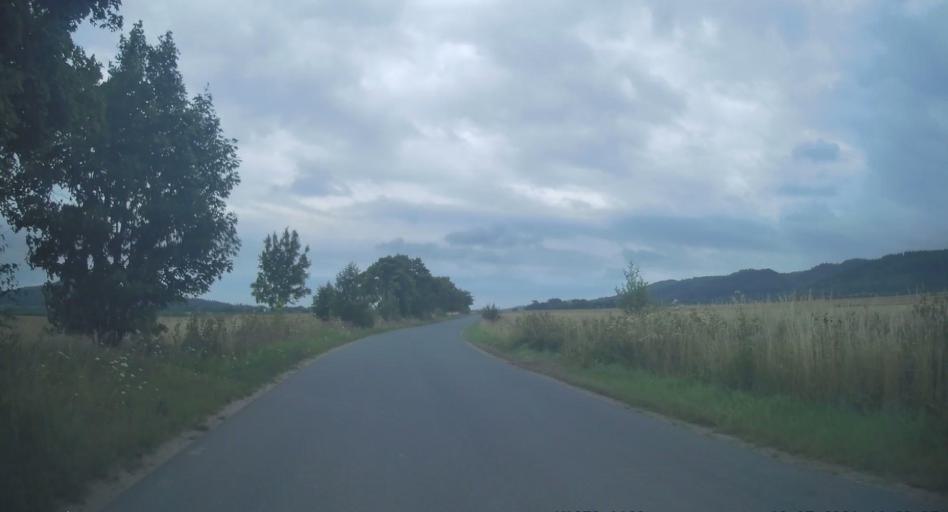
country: PL
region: Lower Silesian Voivodeship
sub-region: Powiat zabkowicki
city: Budzow
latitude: 50.5644
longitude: 16.6871
